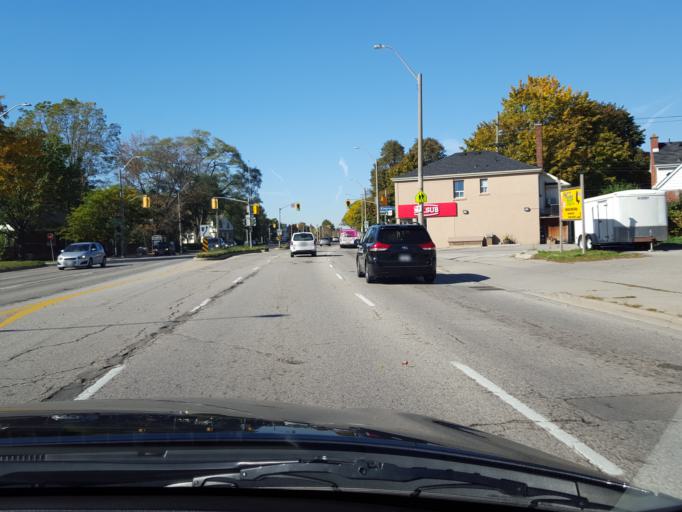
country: CA
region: Ontario
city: Hamilton
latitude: 43.2581
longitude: -79.9109
